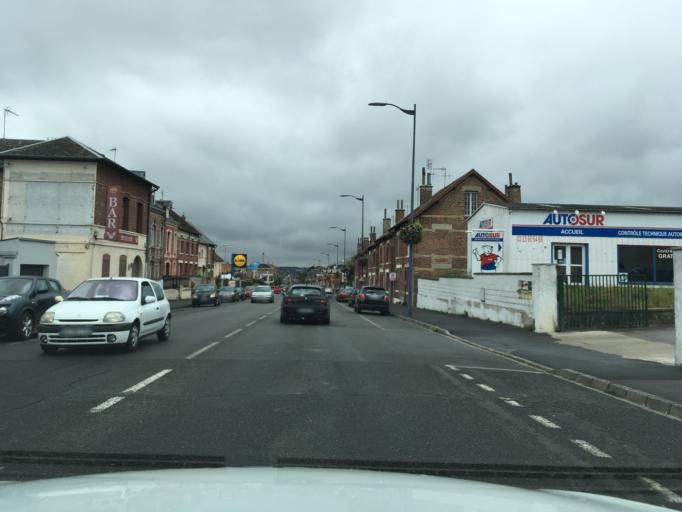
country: FR
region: Picardie
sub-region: Departement de l'Aisne
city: Harly
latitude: 49.8409
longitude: 3.3163
